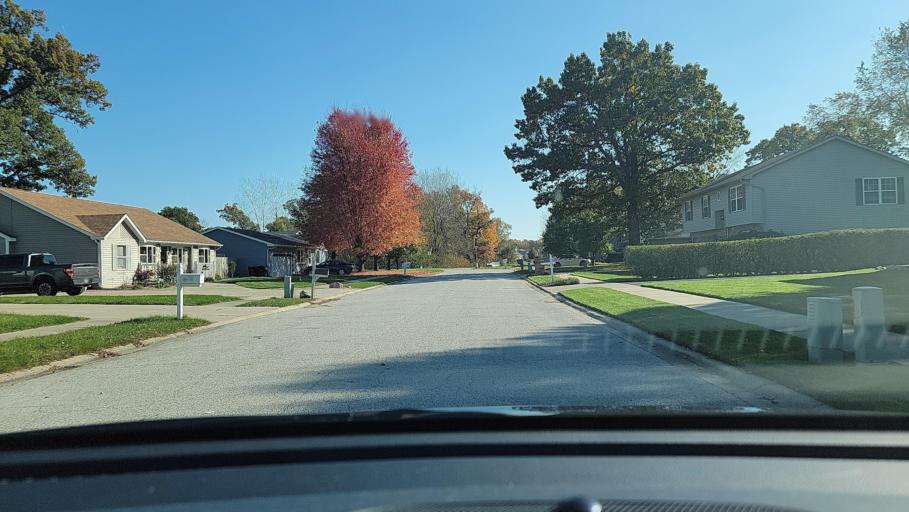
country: US
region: Indiana
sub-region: Porter County
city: Portage
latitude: 41.5792
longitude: -87.1599
